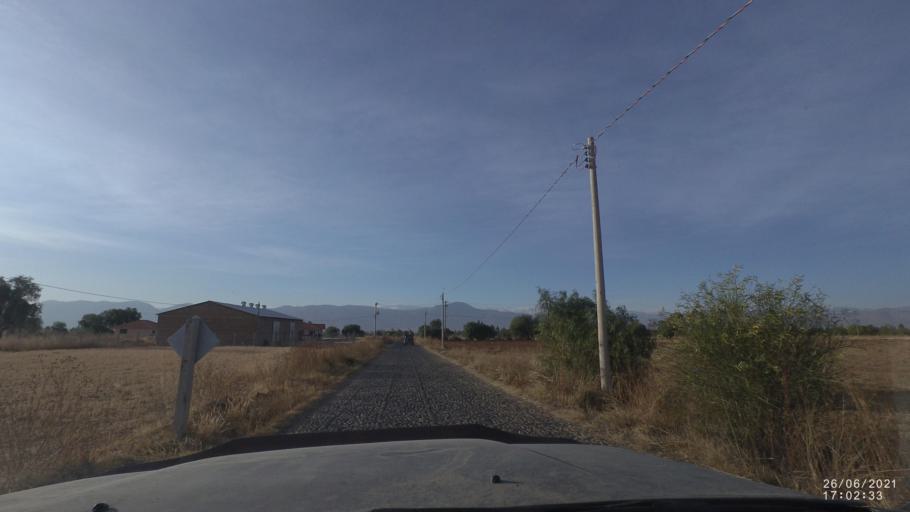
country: BO
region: Cochabamba
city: Cliza
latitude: -17.6528
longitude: -65.9130
